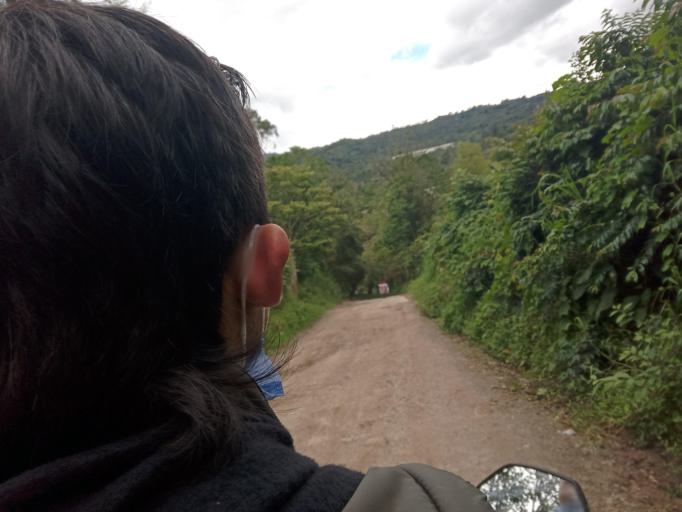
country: CO
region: Cundinamarca
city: Tenza
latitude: 5.1041
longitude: -73.4439
